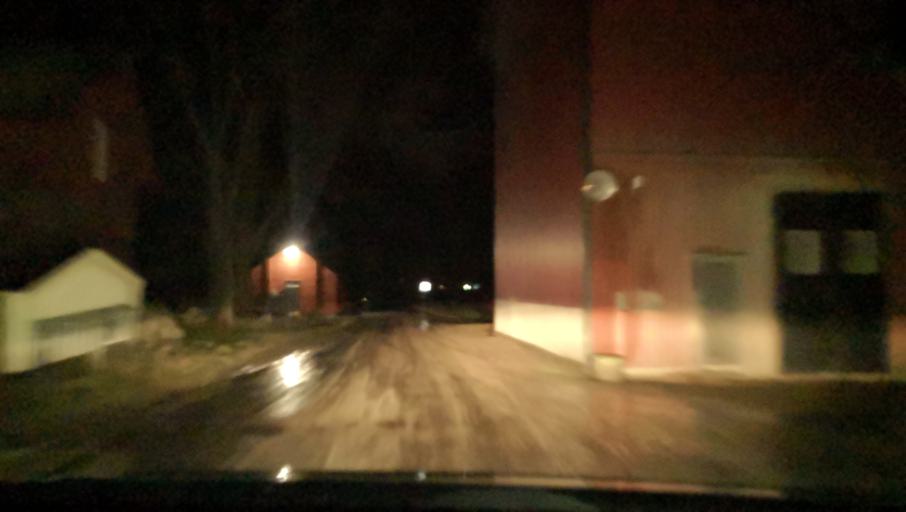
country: SE
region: Vaestmanland
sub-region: Vasteras
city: Tillberga
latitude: 59.6772
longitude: 16.6803
